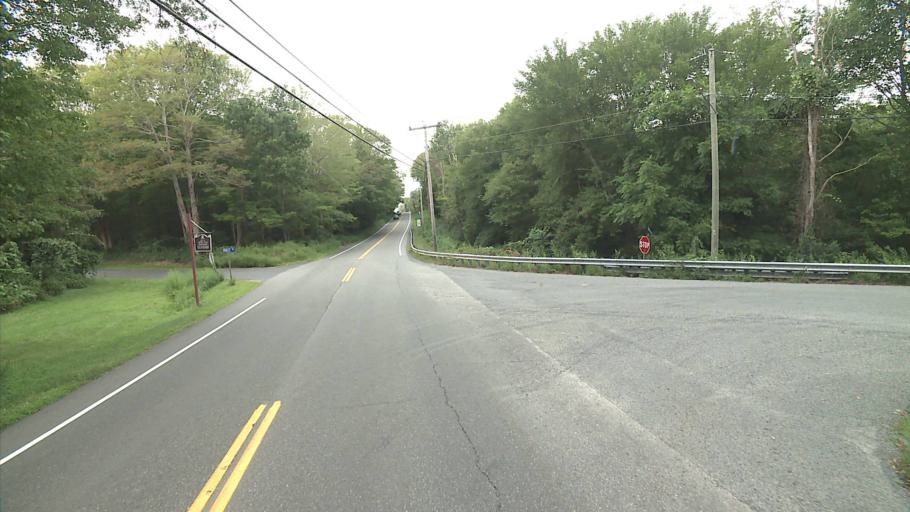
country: US
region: Connecticut
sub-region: New London County
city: Colchester
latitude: 41.4848
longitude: -72.2733
